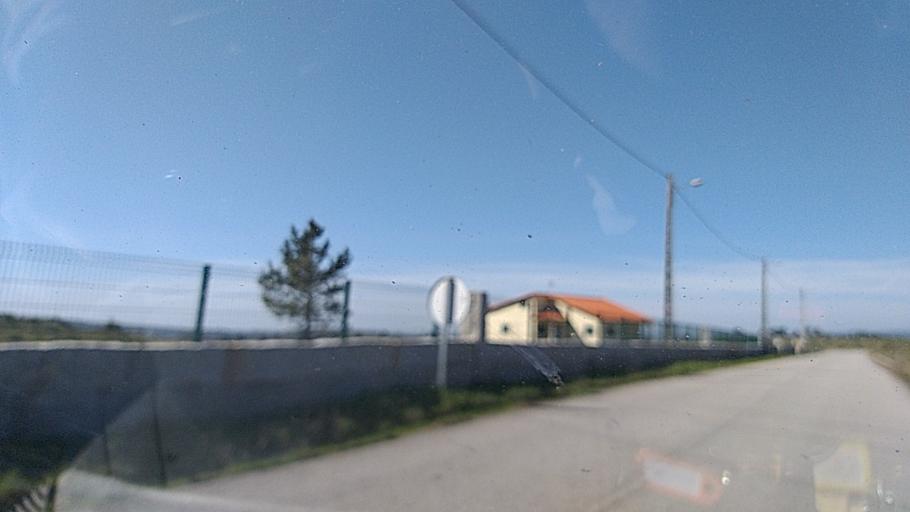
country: PT
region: Guarda
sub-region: Celorico da Beira
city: Celorico da Beira
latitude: 40.5928
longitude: -7.4442
